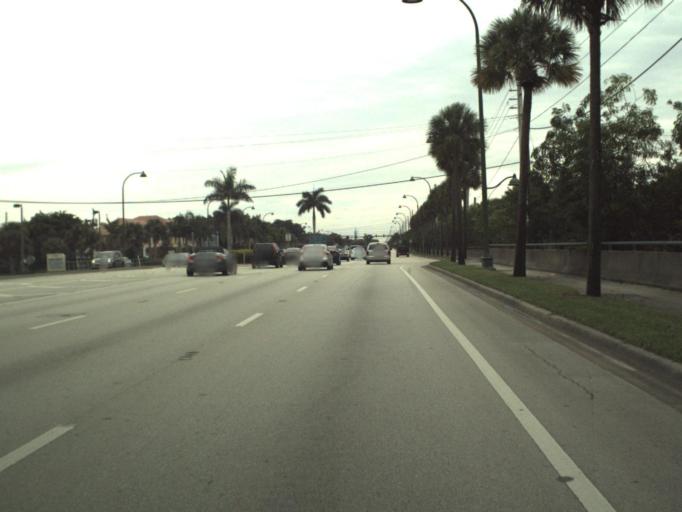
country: US
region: Florida
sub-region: Palm Beach County
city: Wellington
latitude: 26.6812
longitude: -80.2346
